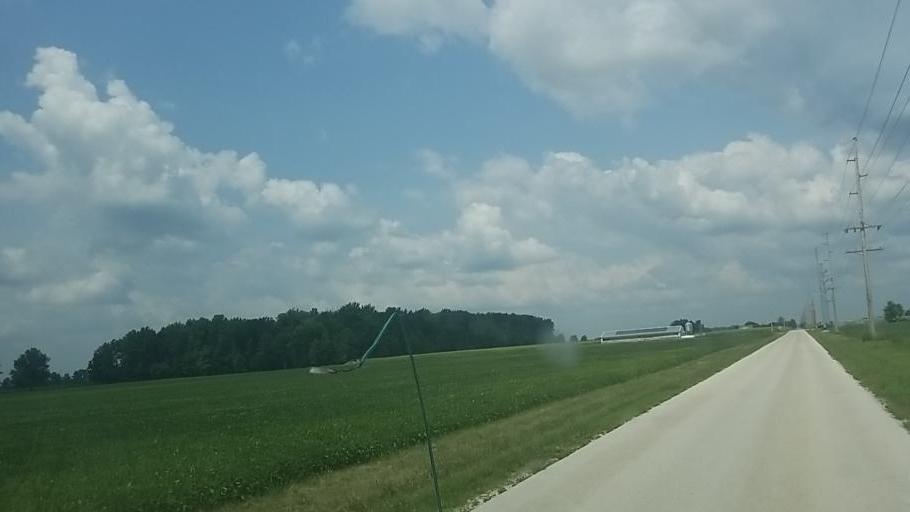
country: US
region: Ohio
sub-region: Wyandot County
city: Carey
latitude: 40.9643
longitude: -83.3048
